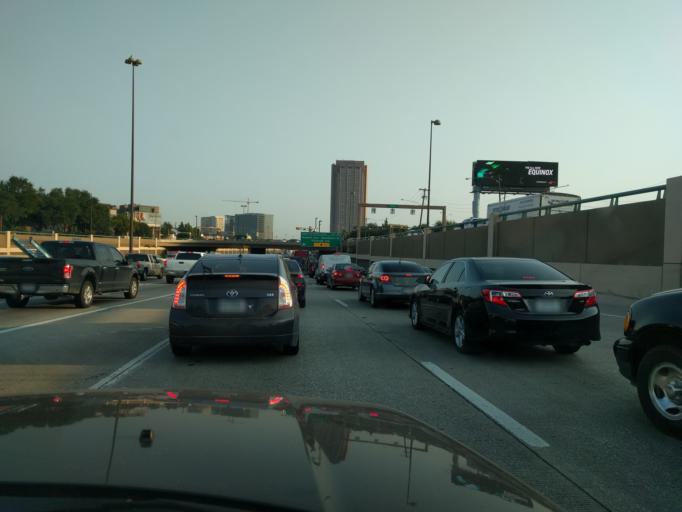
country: US
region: Texas
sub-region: Dallas County
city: Dallas
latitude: 32.7969
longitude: -96.7928
